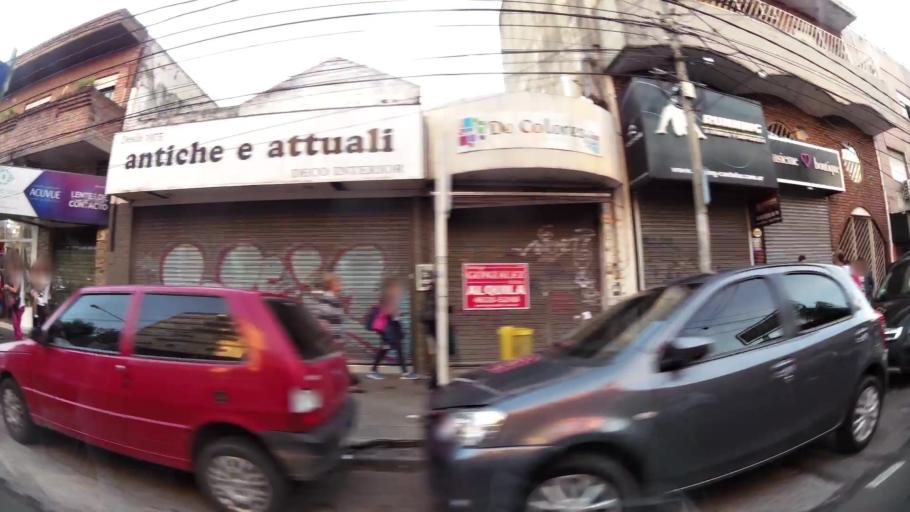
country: AR
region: Buenos Aires
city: Ituzaingo
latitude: -34.6499
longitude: -58.6423
